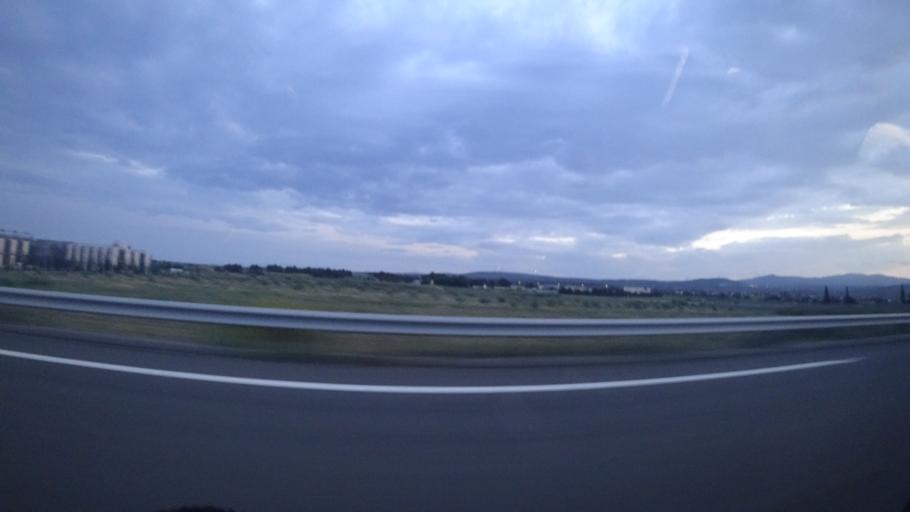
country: FR
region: Languedoc-Roussillon
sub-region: Departement de l'Aude
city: Leucate
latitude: 42.9359
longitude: 2.9934
